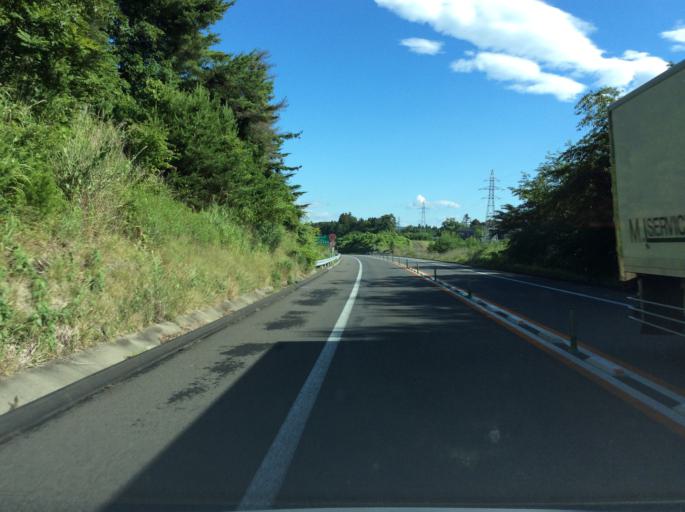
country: JP
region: Fukushima
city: Namie
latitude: 37.2591
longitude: 140.9910
